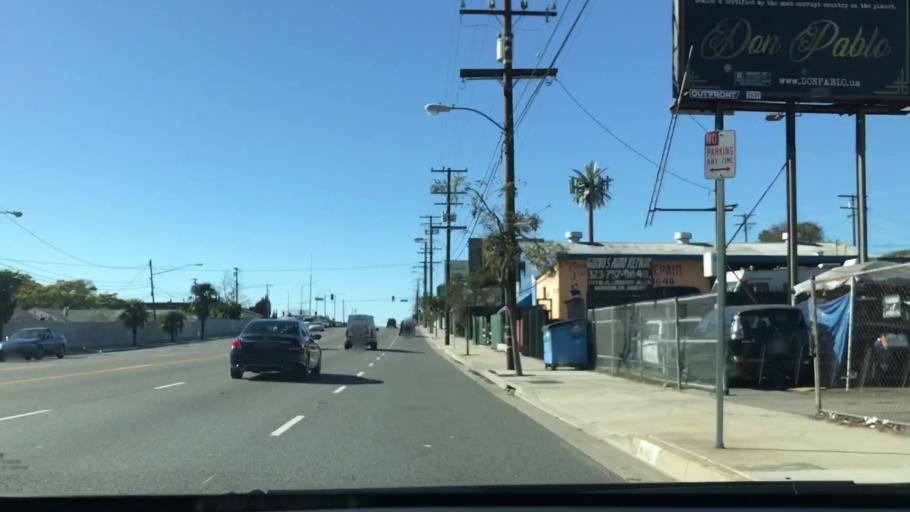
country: US
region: California
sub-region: Los Angeles County
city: West Athens
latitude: 33.9165
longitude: -118.2943
